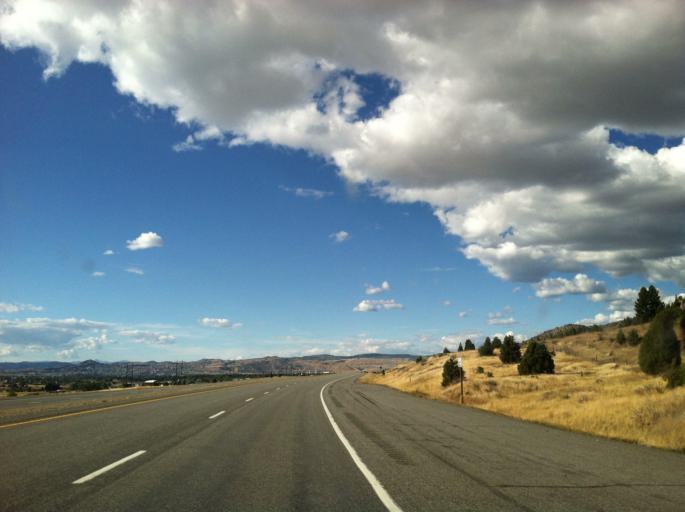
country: US
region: Montana
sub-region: Silver Bow County
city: Butte
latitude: 45.9469
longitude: -112.4650
